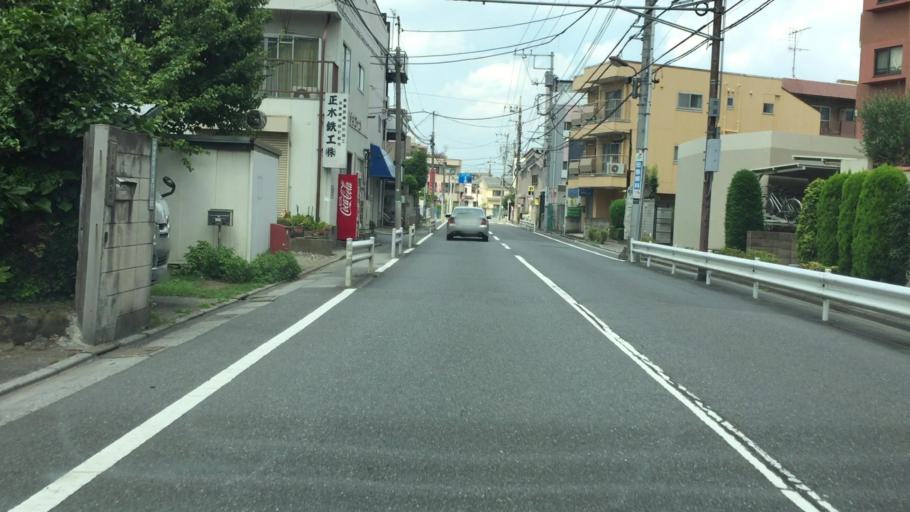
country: JP
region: Saitama
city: Soka
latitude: 35.7693
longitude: 139.8089
